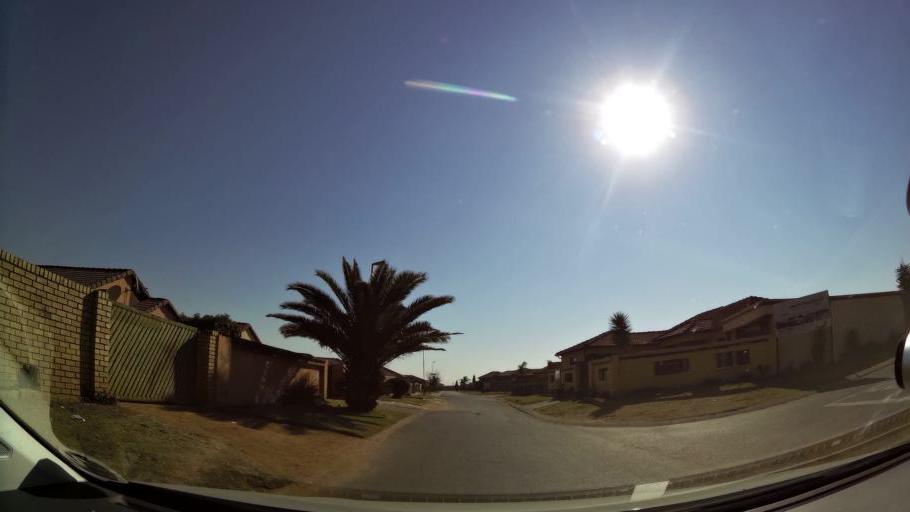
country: ZA
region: Gauteng
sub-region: Ekurhuleni Metropolitan Municipality
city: Tembisa
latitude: -26.0444
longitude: 28.2008
